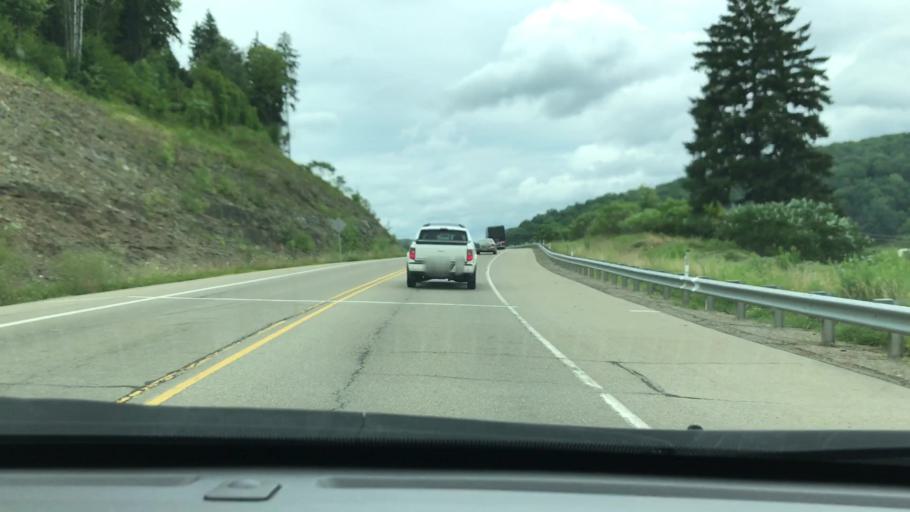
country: US
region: Pennsylvania
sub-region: Elk County
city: Johnsonburg
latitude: 41.4895
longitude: -78.6813
